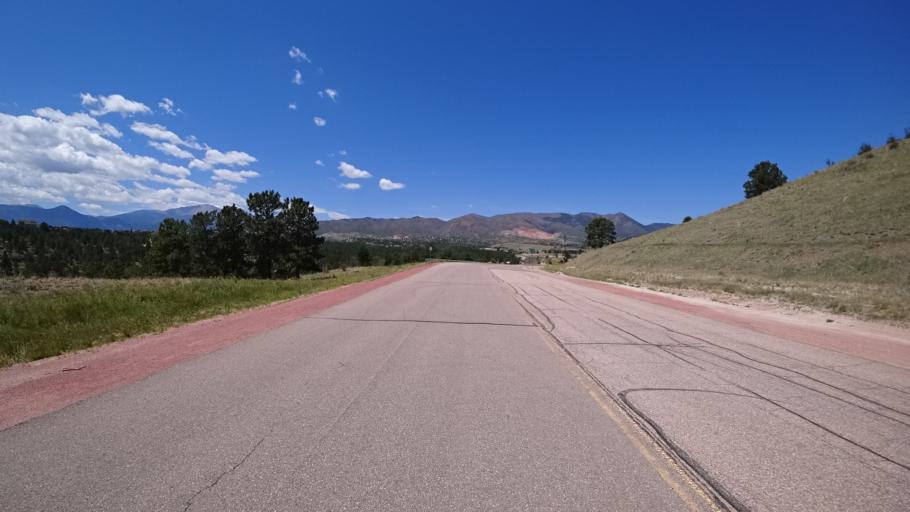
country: US
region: Colorado
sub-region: El Paso County
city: Colorado Springs
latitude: 38.9142
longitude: -104.8345
